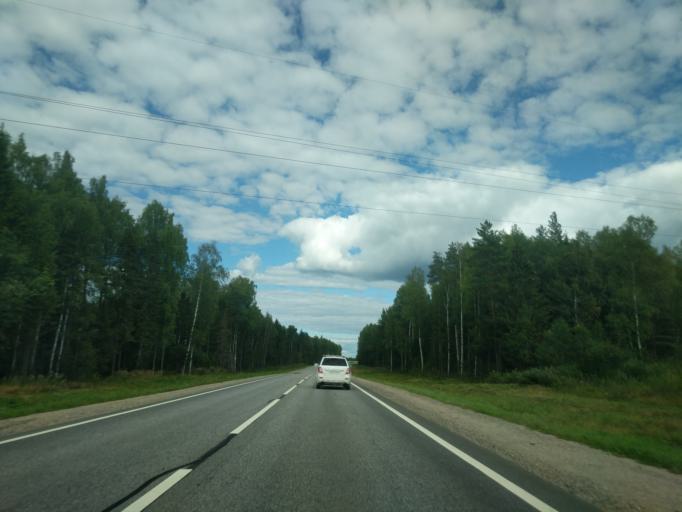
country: RU
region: Kostroma
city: Ostrovskoye
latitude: 57.8103
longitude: 42.4195
